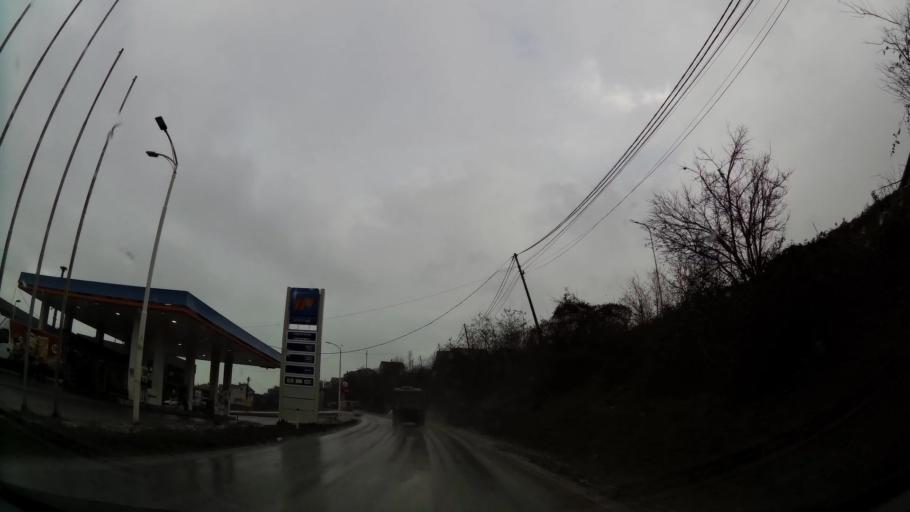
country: XK
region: Ferizaj
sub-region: Komuna e Kacanikut
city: Kacanik
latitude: 42.2316
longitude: 21.2540
